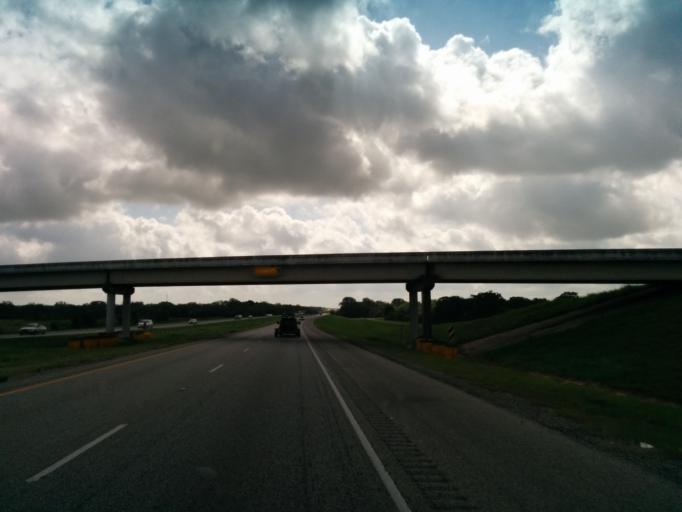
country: US
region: Texas
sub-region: Gonzales County
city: Waelder
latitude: 29.6617
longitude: -97.3895
